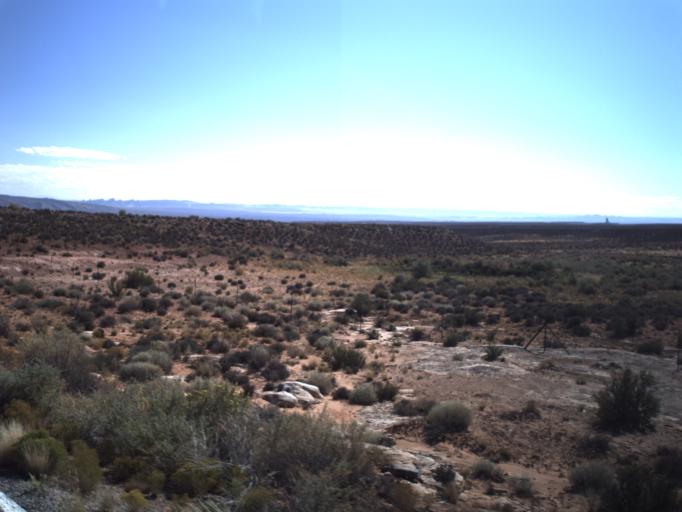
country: US
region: Utah
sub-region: San Juan County
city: Blanding
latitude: 37.2357
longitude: -109.9086
